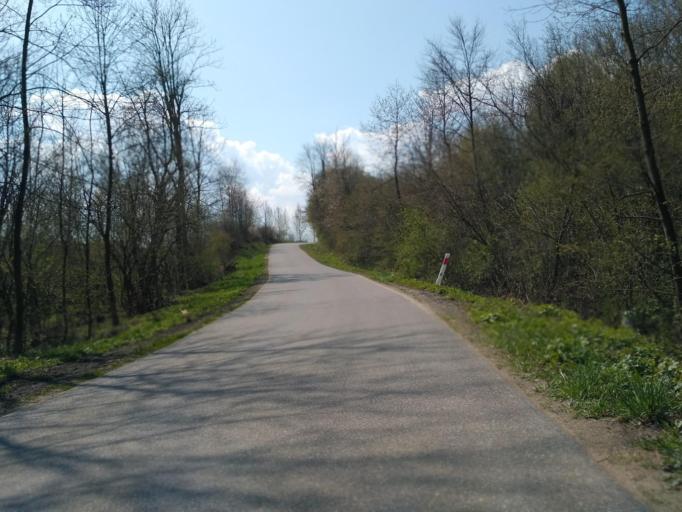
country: PL
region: Subcarpathian Voivodeship
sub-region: Powiat sanocki
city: Zarszyn
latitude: 49.5536
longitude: 21.9898
